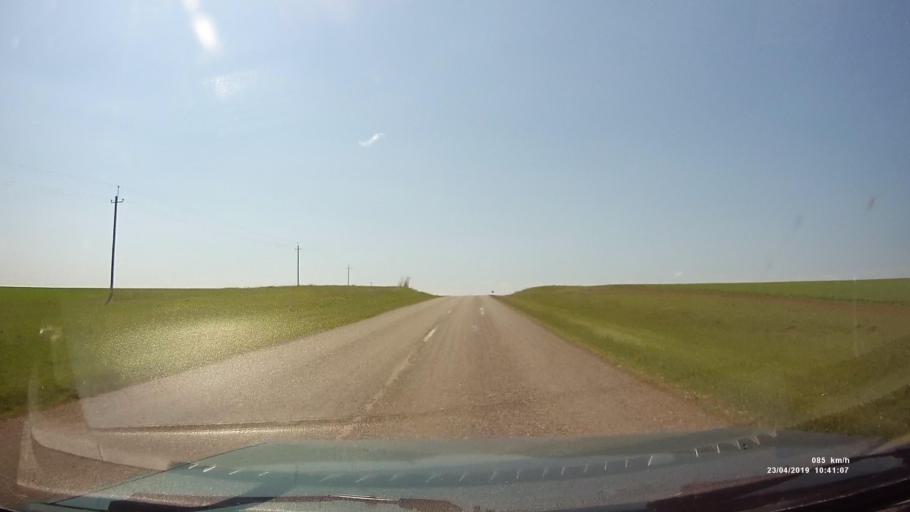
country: RU
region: Kalmykiya
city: Yashalta
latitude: 46.4976
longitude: 42.6383
